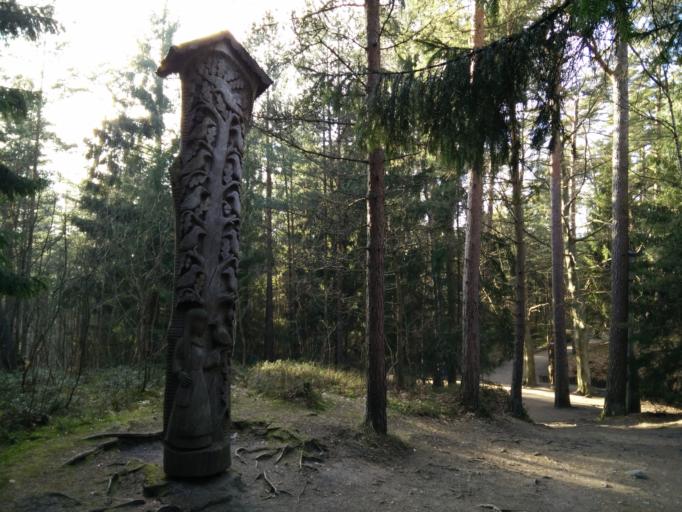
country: LT
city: Neringa
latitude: 55.5356
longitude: 21.1117
